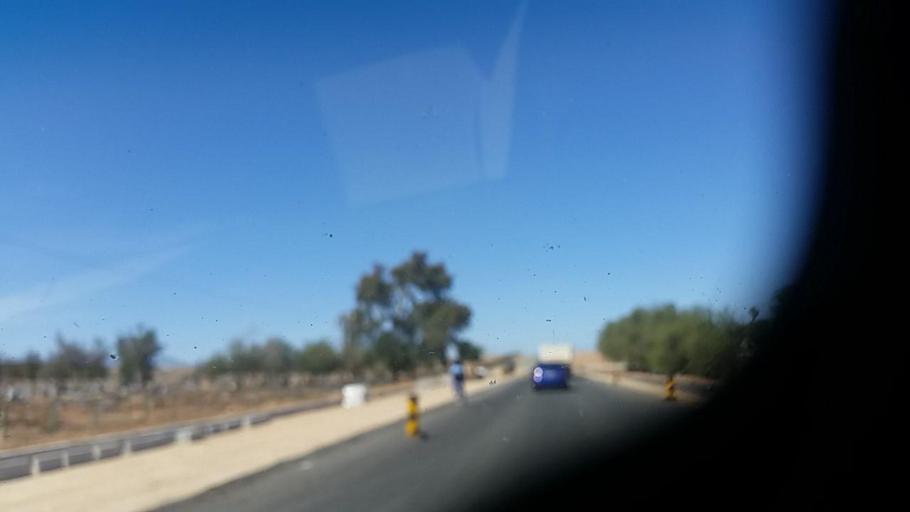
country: ZA
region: Western Cape
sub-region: Eden District Municipality
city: Oudtshoorn
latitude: -33.5930
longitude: 22.2307
